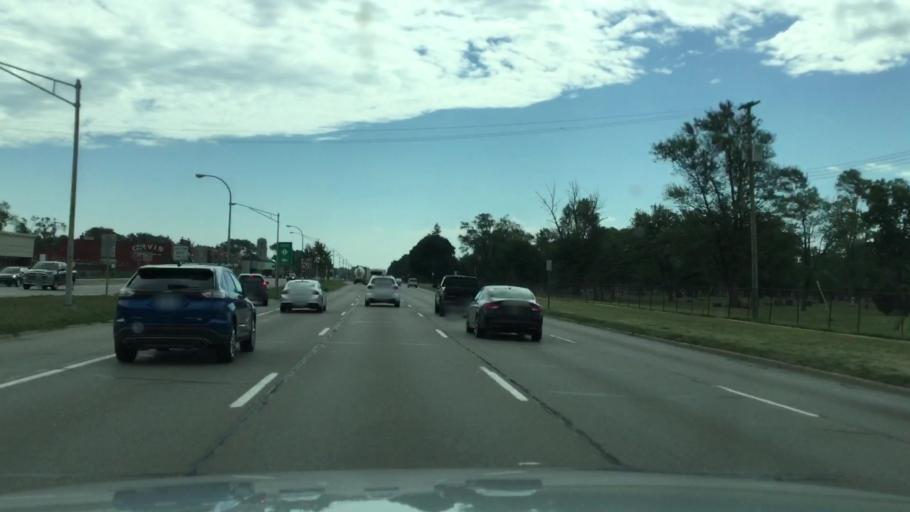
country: US
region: Michigan
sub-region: Oakland County
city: Berkley
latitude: 42.5091
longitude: -83.1779
